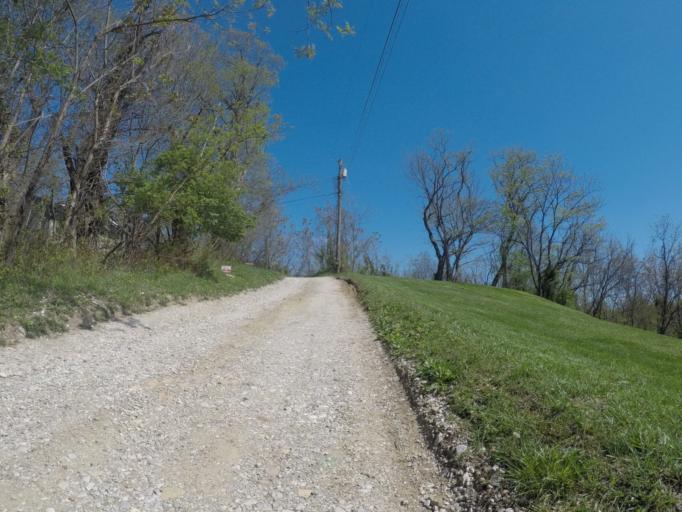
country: US
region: West Virginia
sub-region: Wayne County
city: Kenova
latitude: 38.3897
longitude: -82.5826
